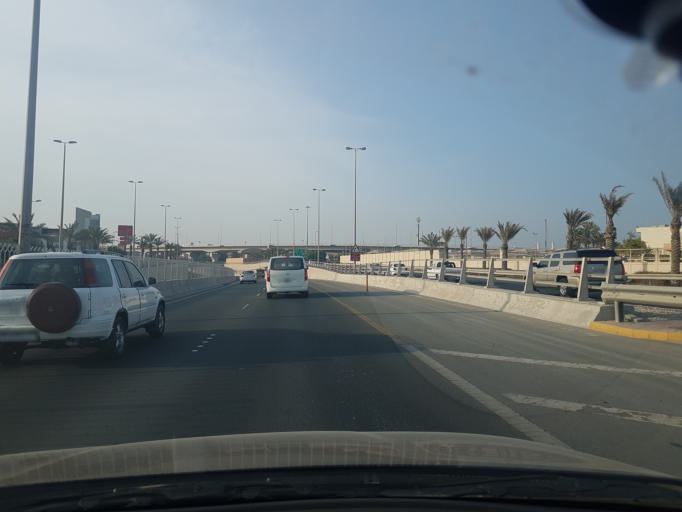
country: BH
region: Northern
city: Madinat `Isa
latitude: 26.1658
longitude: 50.5429
